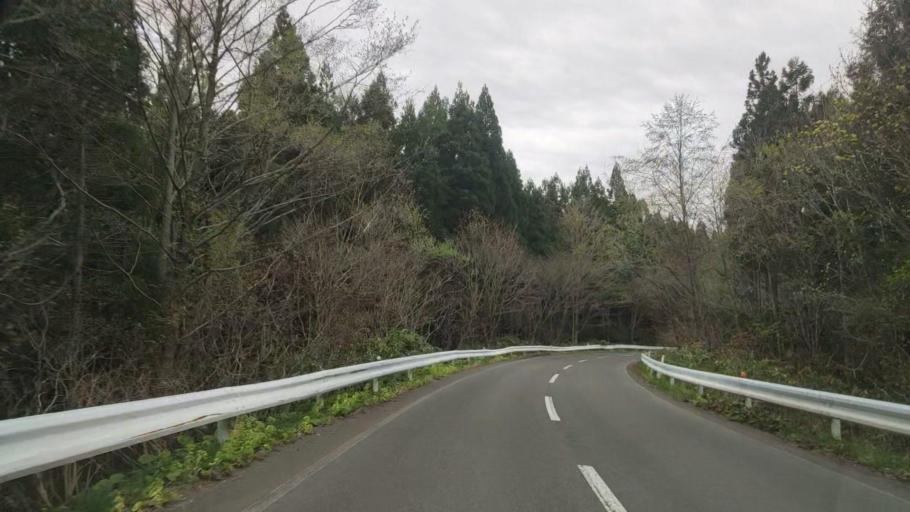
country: JP
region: Akita
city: Hanawa
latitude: 40.3973
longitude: 140.8000
